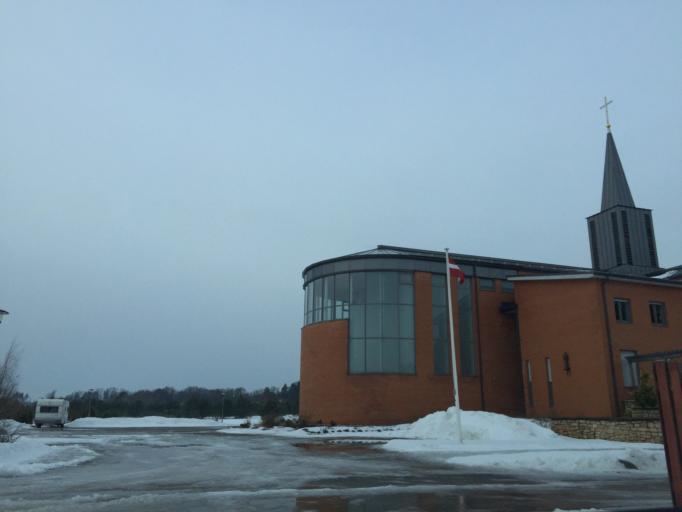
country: LV
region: Ikskile
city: Ikskile
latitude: 56.8409
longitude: 24.4778
